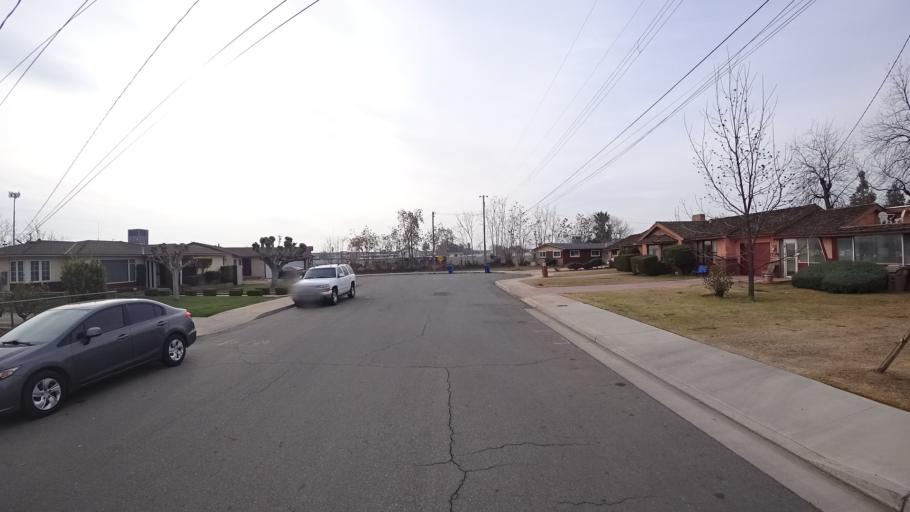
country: US
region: California
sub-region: Kern County
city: Bakersfield
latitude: 35.3555
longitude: -119.0131
